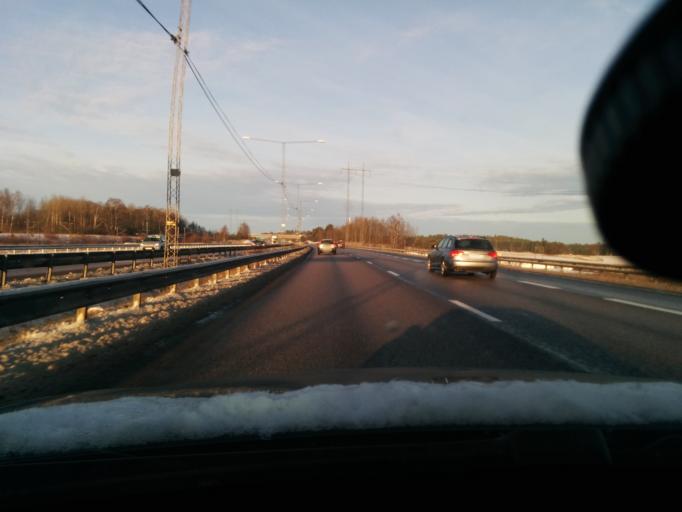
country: SE
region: Stockholm
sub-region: Sigtuna Kommun
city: Rosersberg
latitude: 59.5789
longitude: 17.9012
